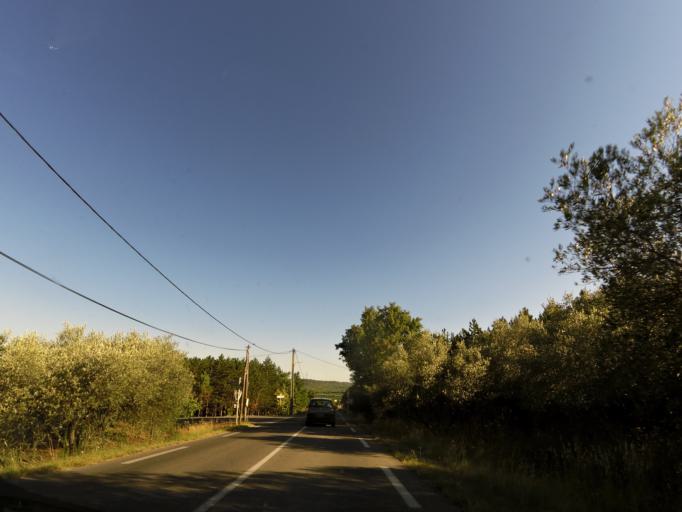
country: FR
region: Languedoc-Roussillon
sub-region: Departement du Gard
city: Quissac
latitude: 43.8419
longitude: 4.0289
